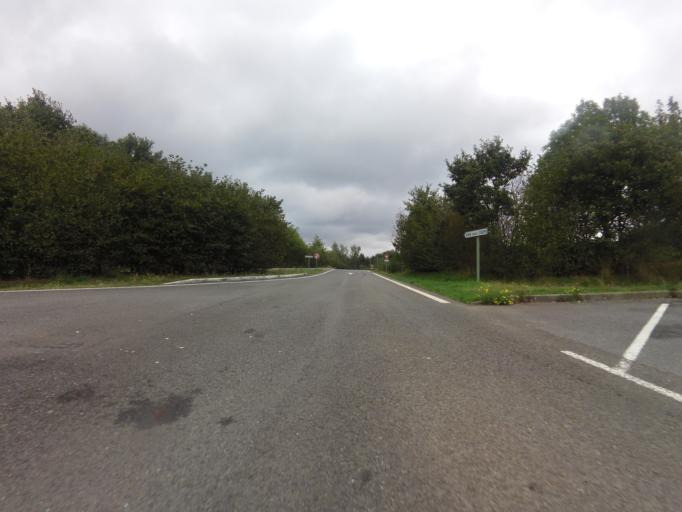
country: FR
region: Brittany
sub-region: Departement d'Ille-et-Vilaine
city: Saint-Sauveur-des-Landes
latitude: 48.3174
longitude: -1.3261
